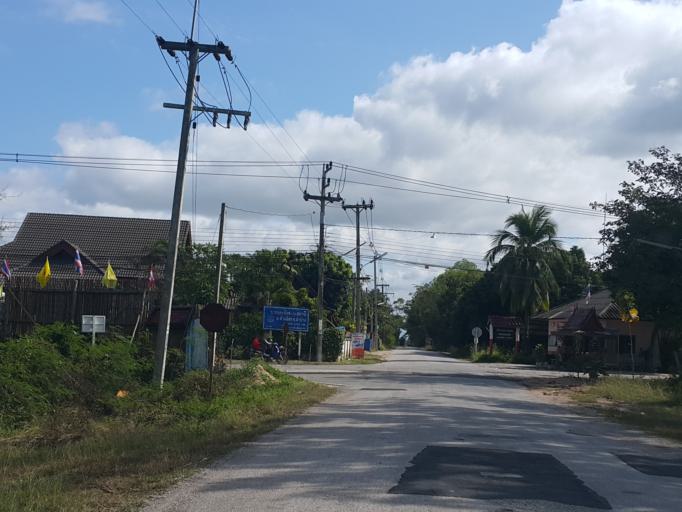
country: TH
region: Lampang
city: Hang Chat
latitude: 18.3460
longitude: 99.3748
